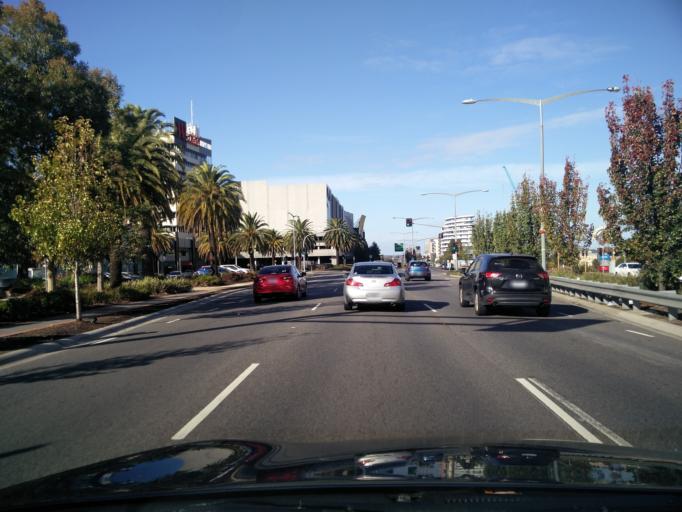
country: AU
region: Victoria
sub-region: Manningham
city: Doncaster
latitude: -37.7838
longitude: 145.1243
